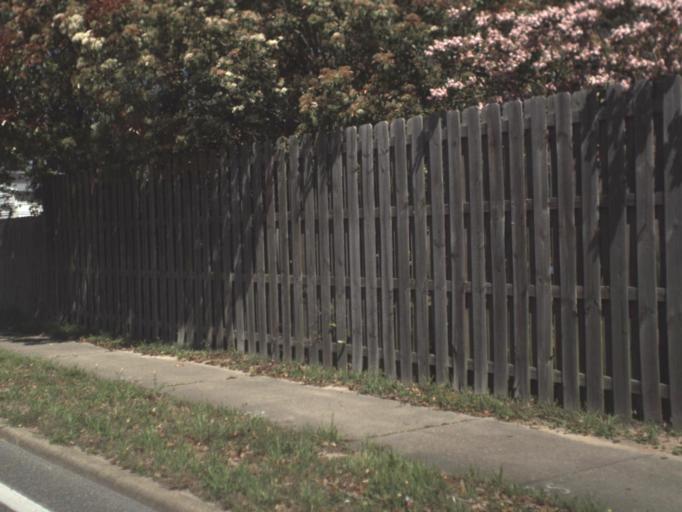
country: US
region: Florida
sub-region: Okaloosa County
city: Mary Esther
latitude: 30.4084
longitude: -86.6440
